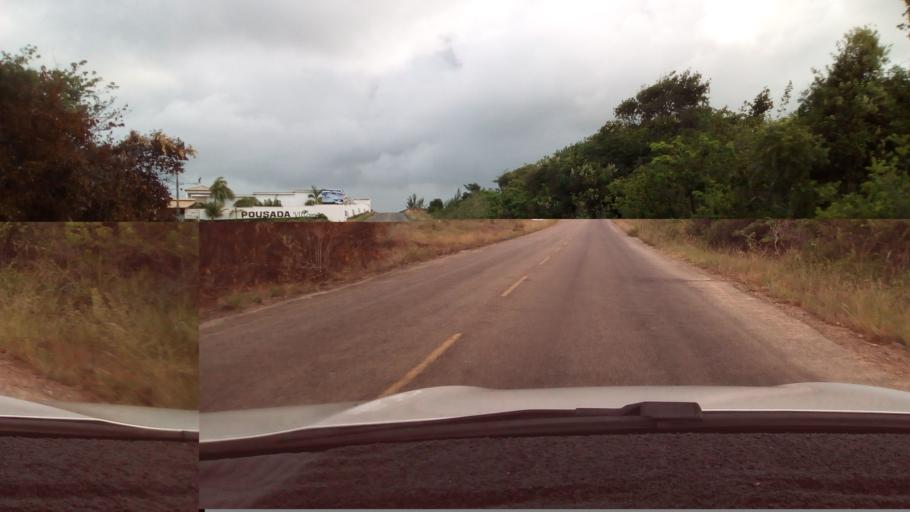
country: BR
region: Paraiba
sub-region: Conde
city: Conde
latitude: -7.3206
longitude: -34.8076
